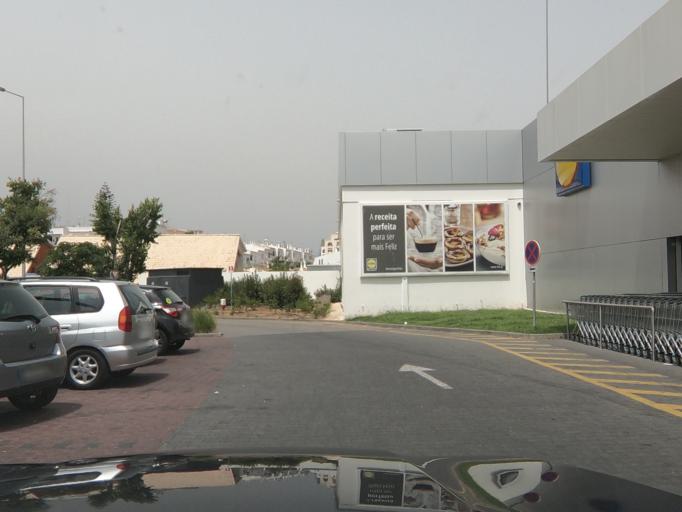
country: PT
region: Faro
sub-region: Portimao
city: Portimao
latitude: 37.1342
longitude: -8.5462
